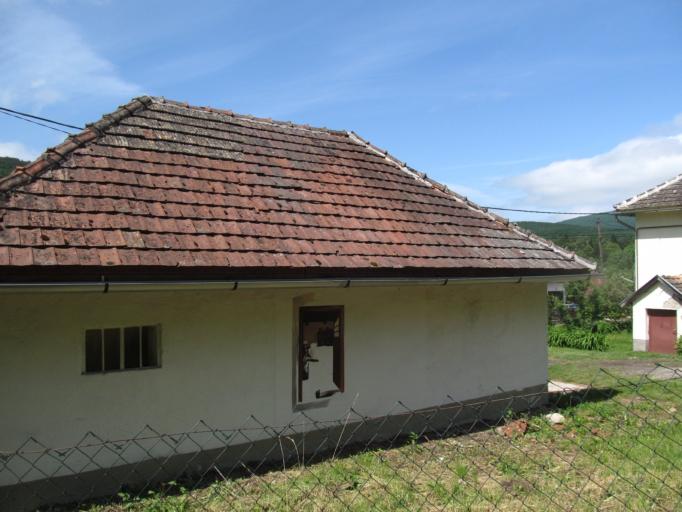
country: HU
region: Borsod-Abauj-Zemplen
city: Gonc
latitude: 48.5399
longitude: 21.4165
